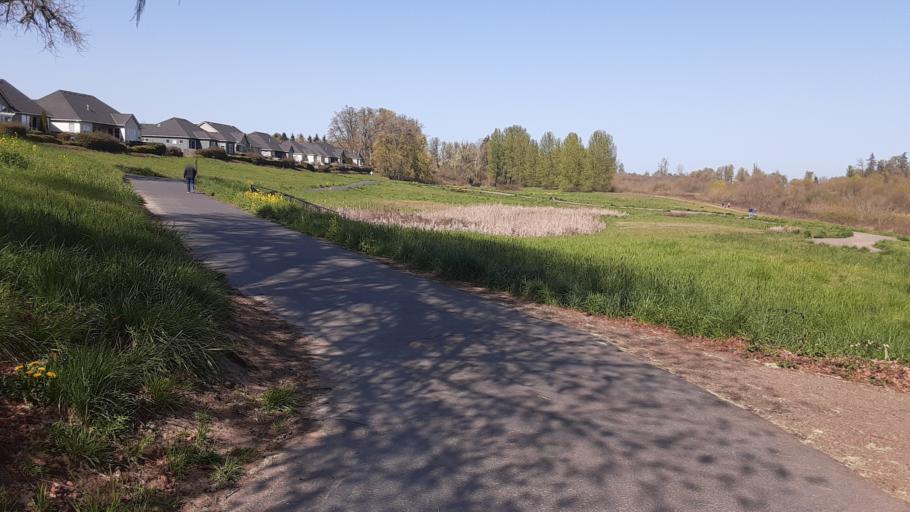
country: US
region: Oregon
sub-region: Benton County
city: Corvallis
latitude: 44.5289
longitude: -123.2550
